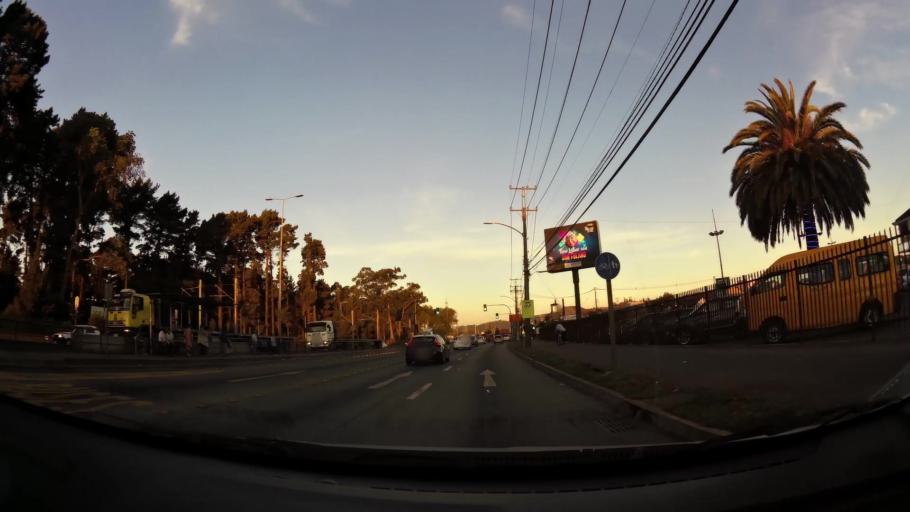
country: CL
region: Biobio
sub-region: Provincia de Concepcion
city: Concepcion
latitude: -36.8388
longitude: -73.0964
